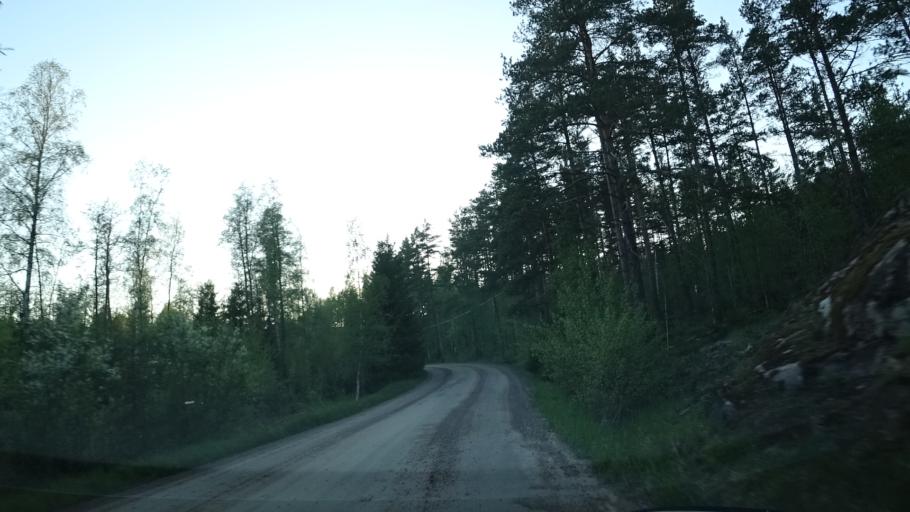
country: FI
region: Uusimaa
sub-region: Helsinki
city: Siuntio
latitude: 60.0626
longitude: 24.2315
